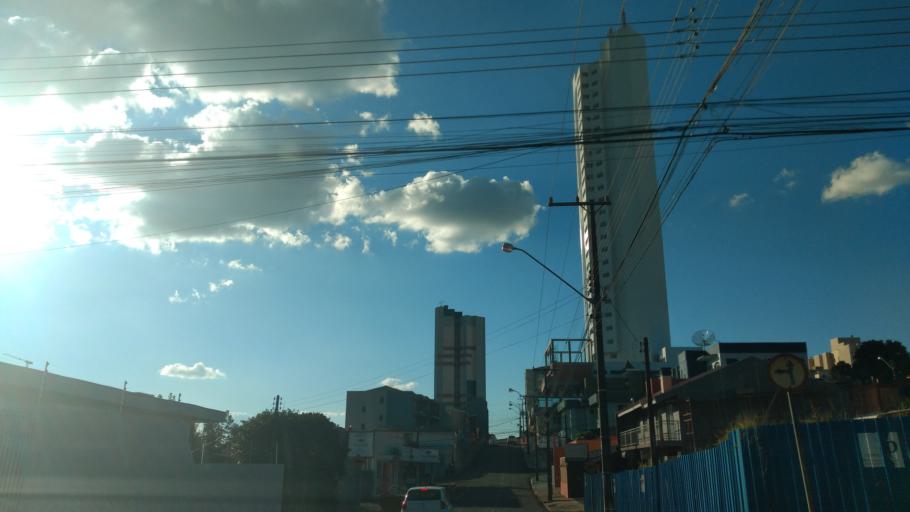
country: BR
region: Parana
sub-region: Guarapuava
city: Guarapuava
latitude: -25.3984
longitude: -51.4676
